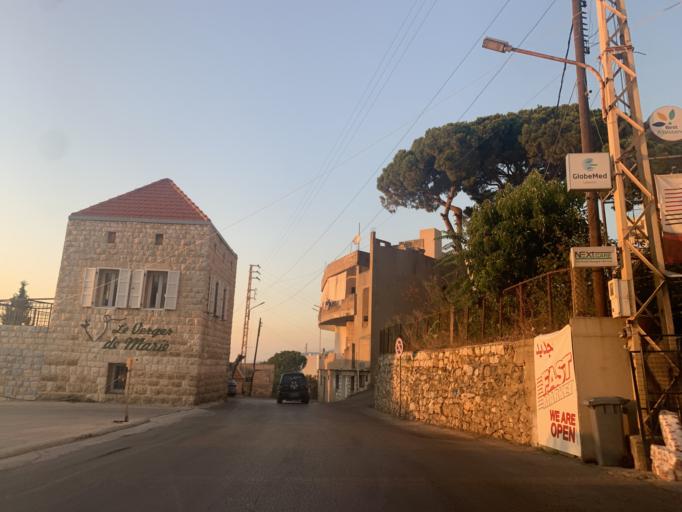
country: LB
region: Mont-Liban
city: Djounie
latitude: 33.9701
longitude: 35.6256
